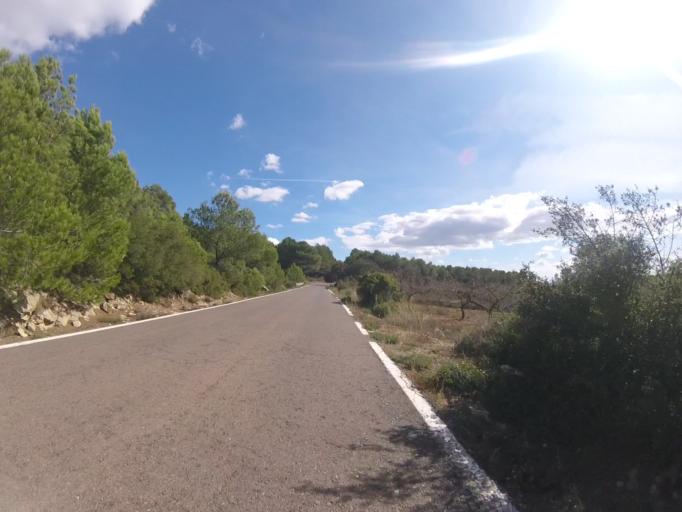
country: ES
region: Valencia
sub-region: Provincia de Castello
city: Albocasser
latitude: 40.4050
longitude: 0.0783
